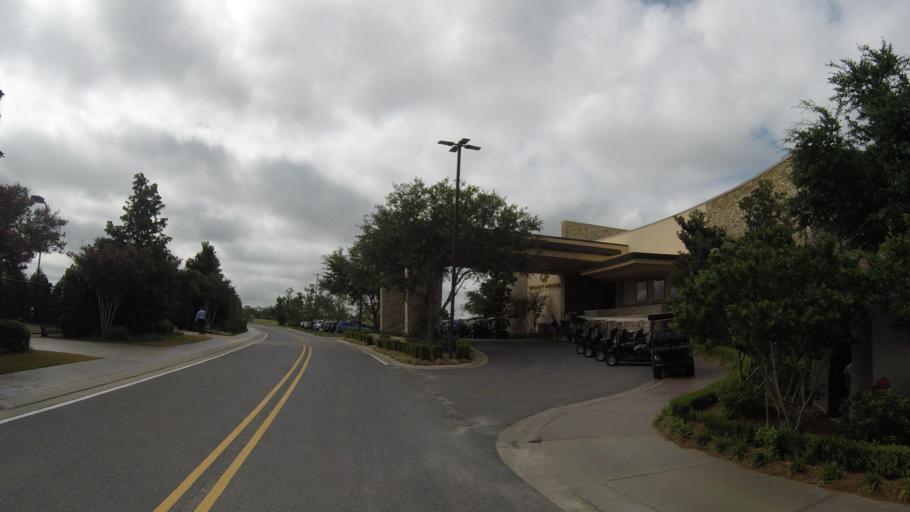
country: US
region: Louisiana
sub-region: Calcasieu Parish
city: Prien
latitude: 30.2039
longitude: -93.2663
